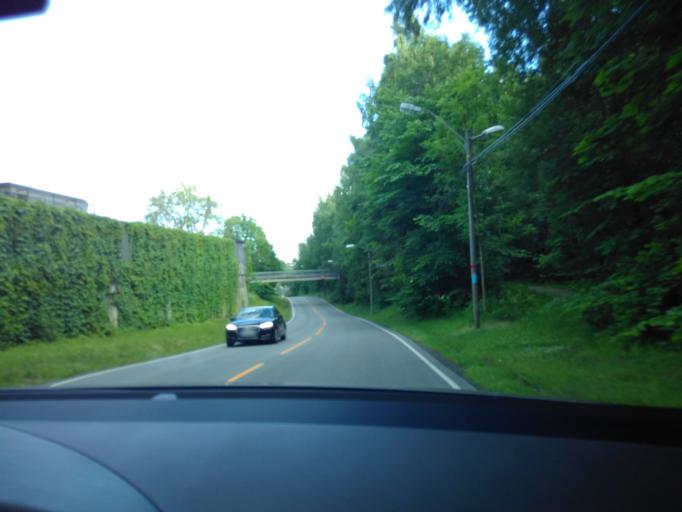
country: NO
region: Akershus
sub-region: Baerum
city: Lysaker
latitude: 59.9395
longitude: 10.6039
